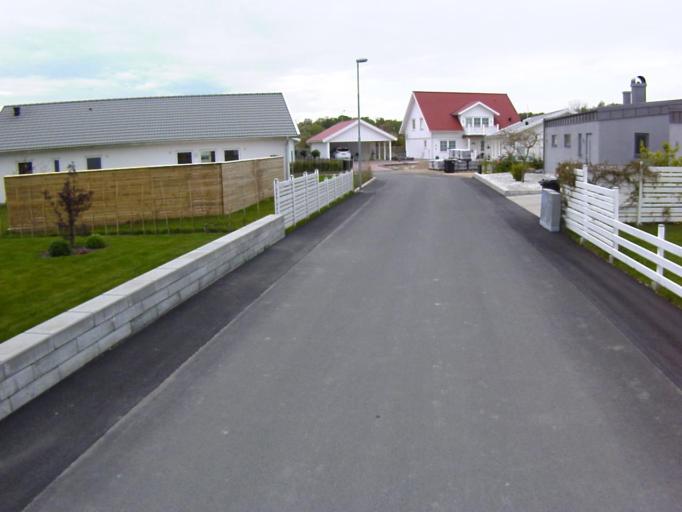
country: SE
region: Skane
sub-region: Kristianstads Kommun
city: Kristianstad
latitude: 56.0194
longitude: 14.1954
